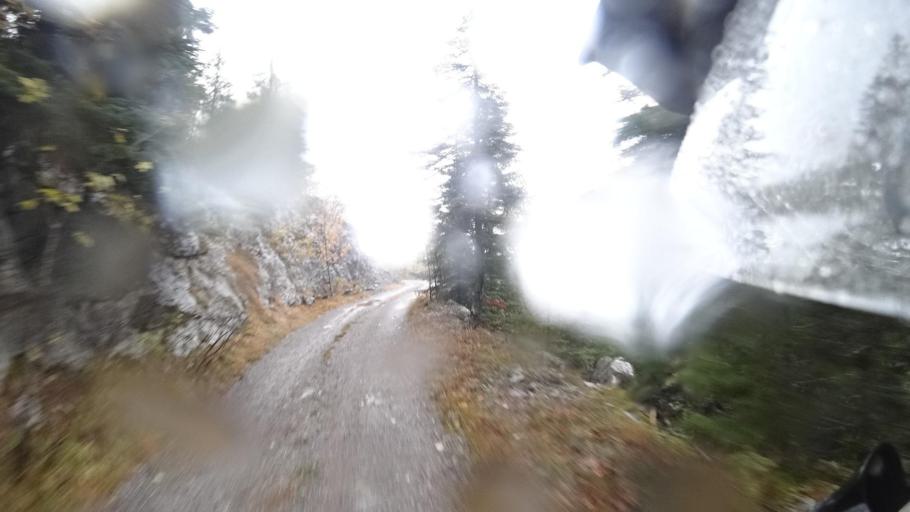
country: HR
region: Primorsko-Goranska
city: Vrbovsko
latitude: 45.2974
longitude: 15.0282
